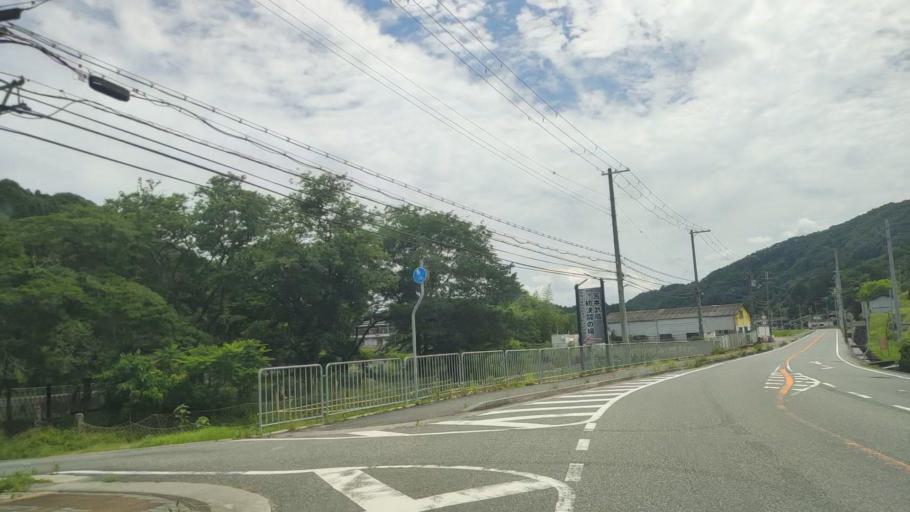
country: JP
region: Hyogo
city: Yamazakicho-nakabirose
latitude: 35.0404
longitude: 134.3693
